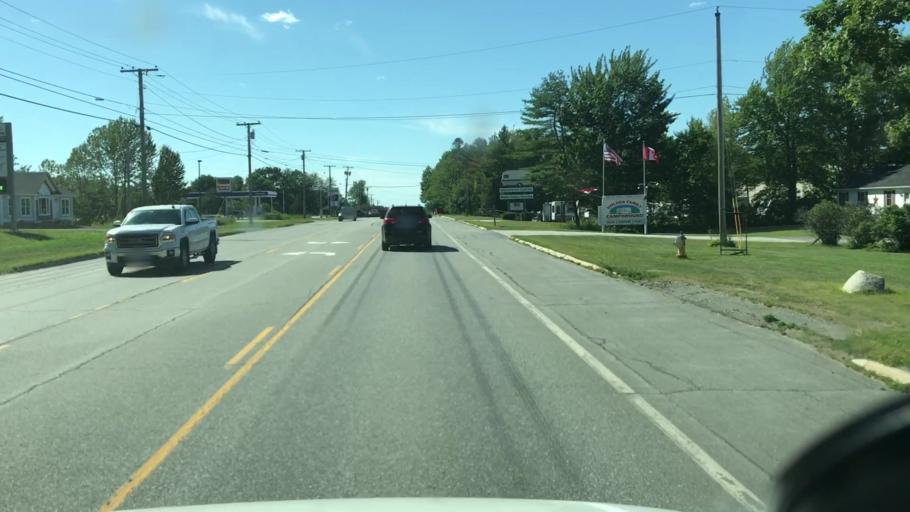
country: US
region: Maine
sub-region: Penobscot County
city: Holden
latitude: 44.7637
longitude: -68.7034
